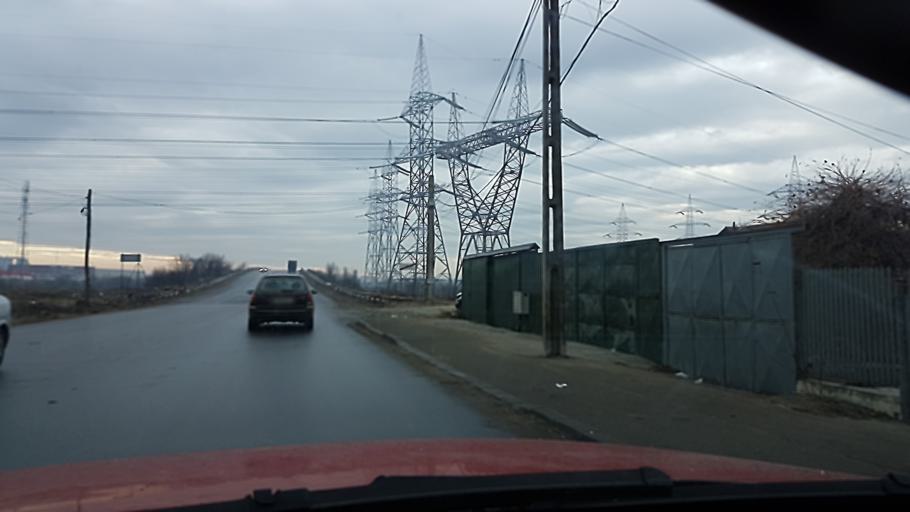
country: RO
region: Ilfov
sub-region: Comuna Glina
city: Catelu
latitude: 44.4017
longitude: 26.2203
